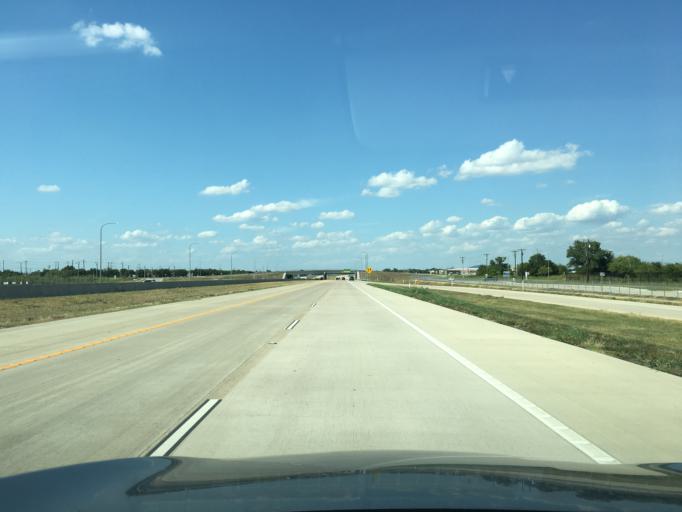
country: US
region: Texas
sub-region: Tarrant County
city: Mansfield
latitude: 32.6047
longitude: -97.0769
